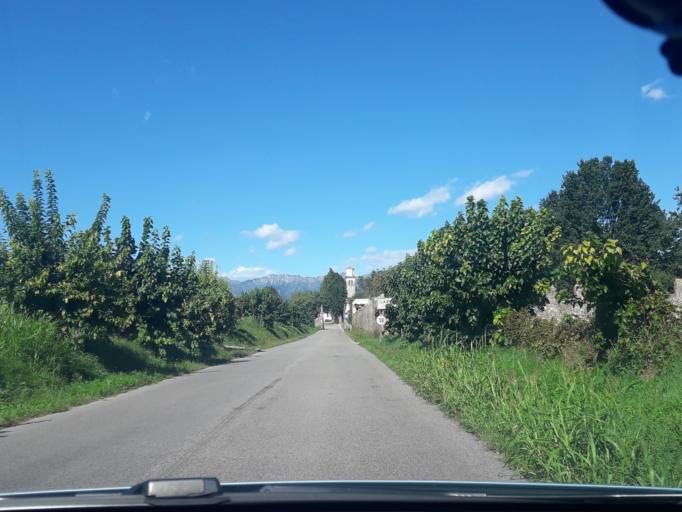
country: IT
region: Friuli Venezia Giulia
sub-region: Provincia di Udine
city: Reana del Roiale
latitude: 46.1472
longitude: 13.2153
